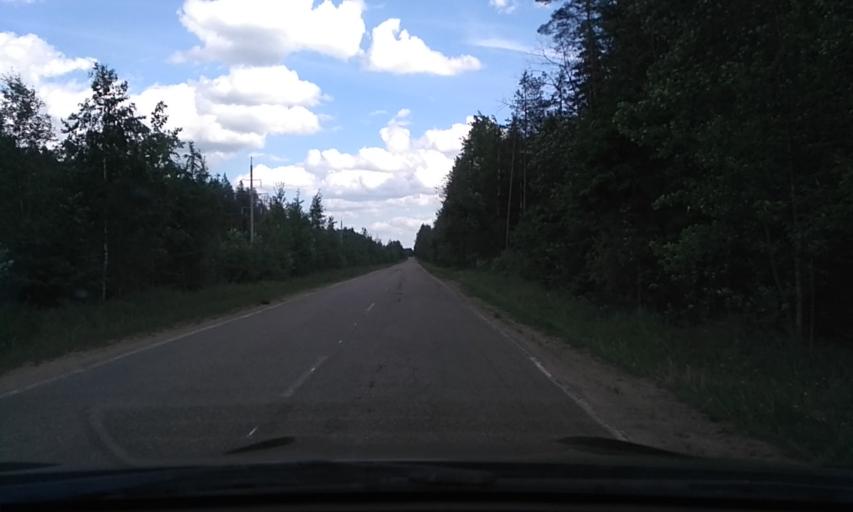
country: RU
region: Leningrad
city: Otradnoye
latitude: 59.8198
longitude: 30.8093
